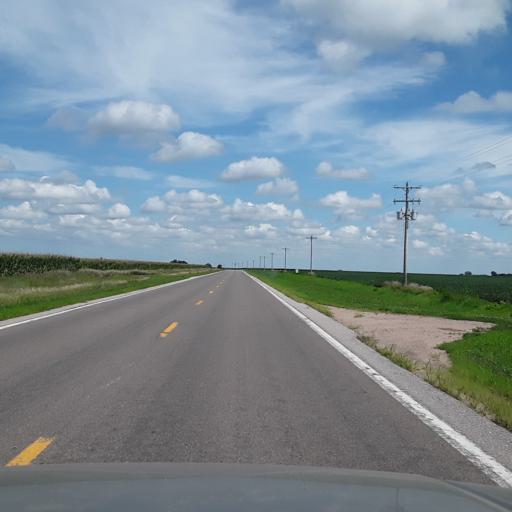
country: US
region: Nebraska
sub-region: Polk County
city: Osceola
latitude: 41.0640
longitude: -97.4063
